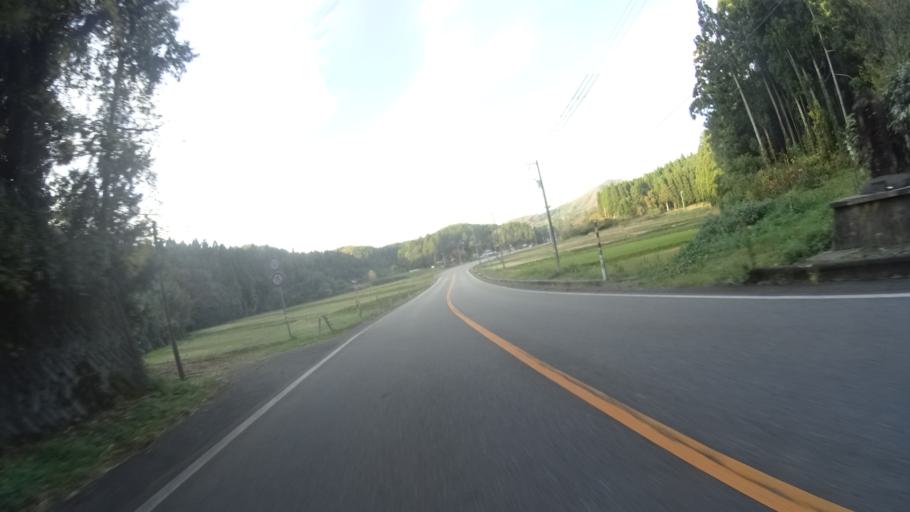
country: JP
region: Ishikawa
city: Nanao
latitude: 37.1839
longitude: 136.7142
